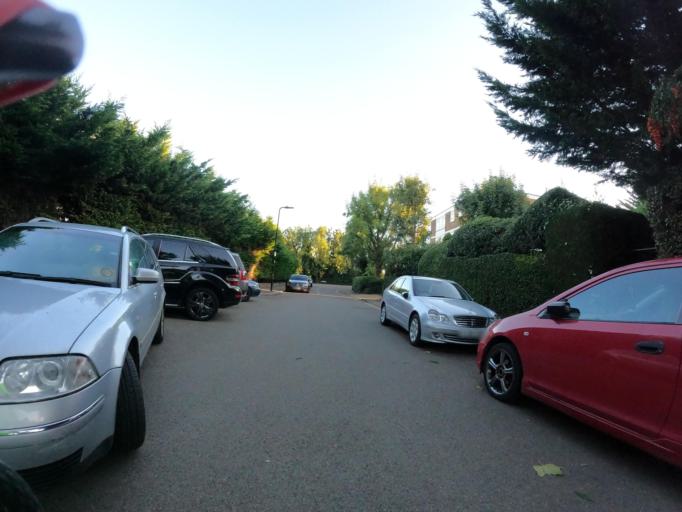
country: GB
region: England
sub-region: Greater London
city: Ealing Broadway
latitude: 51.5331
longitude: -0.3237
